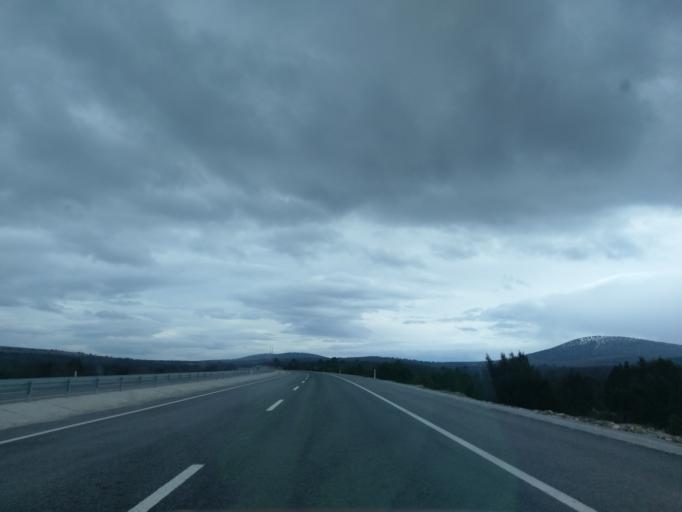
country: TR
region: Kuetahya
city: Cavdarhisar
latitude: 39.2227
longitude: 29.7339
